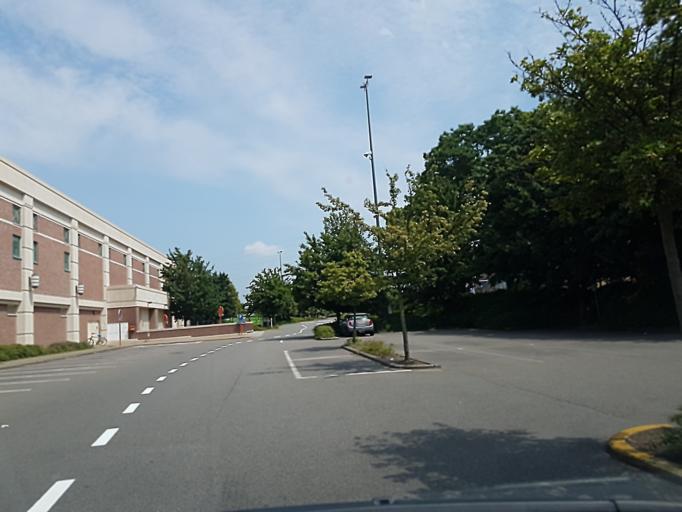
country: BE
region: Flanders
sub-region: Provincie Antwerpen
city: Wijnegem
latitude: 51.2227
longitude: 4.5037
